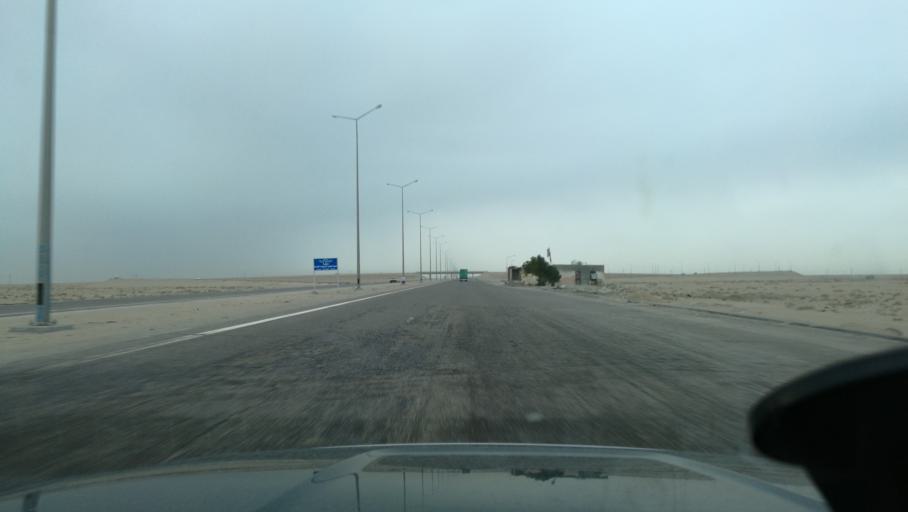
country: IQ
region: Dhi Qar
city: Suq ash Shuyukh
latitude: 30.6684
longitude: 46.5328
